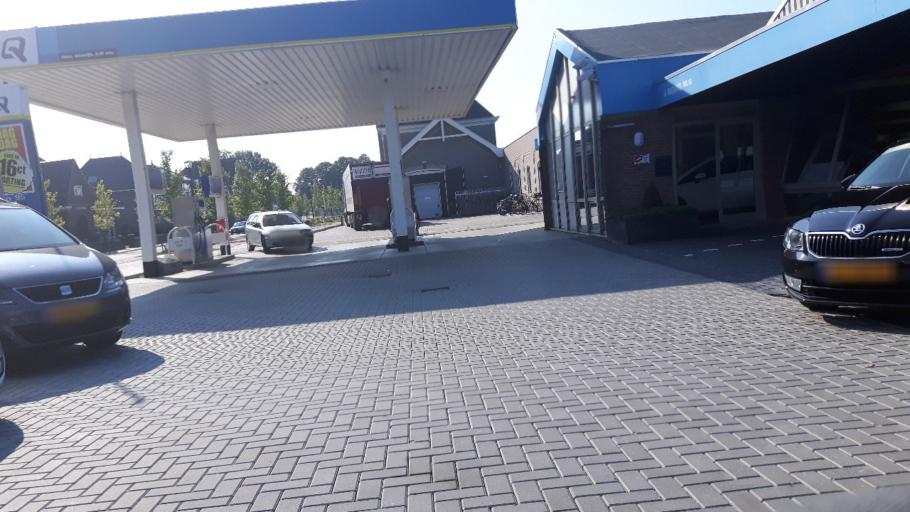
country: NL
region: Friesland
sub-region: Gemeente Franekeradeel
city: Franeker
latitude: 53.1874
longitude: 5.5518
